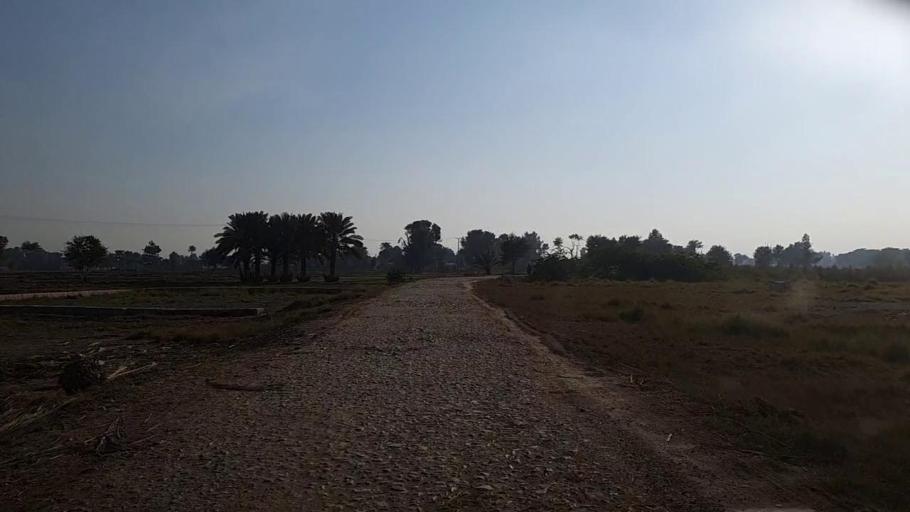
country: PK
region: Sindh
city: Ranipur
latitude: 27.2459
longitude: 68.5404
